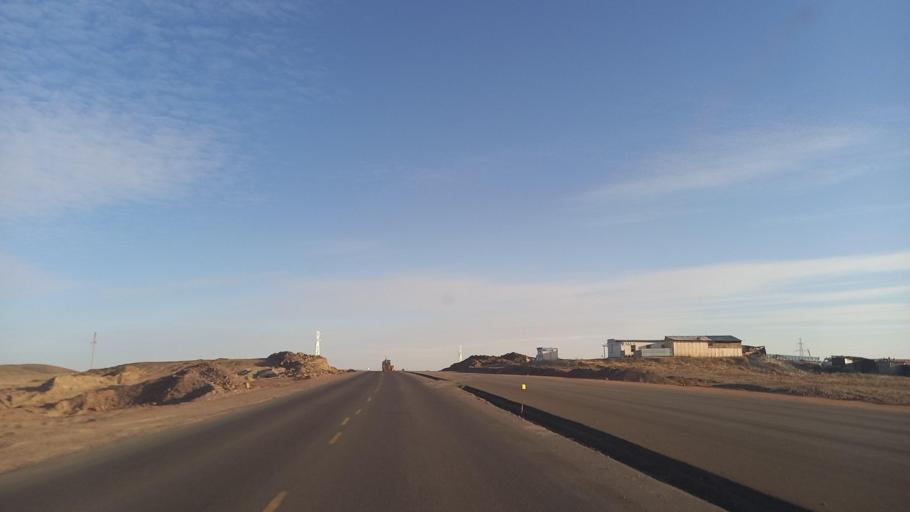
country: KZ
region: Zhambyl
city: Mynaral
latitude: 45.3447
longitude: 73.6971
